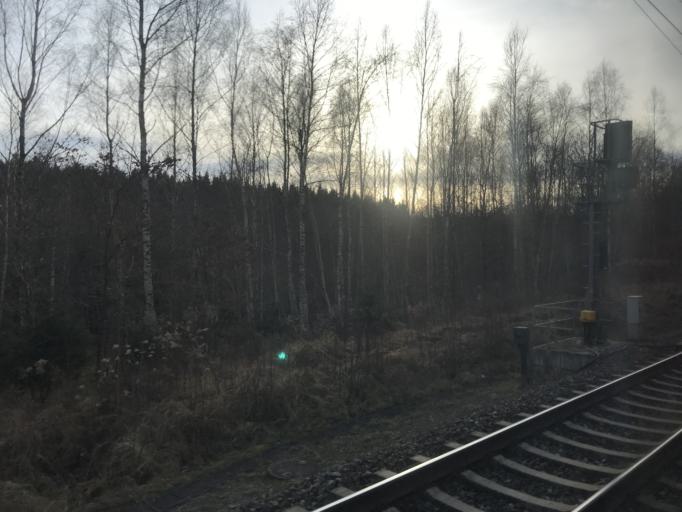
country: DE
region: Bavaria
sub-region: Swabia
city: Rosshaupten
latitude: 48.3948
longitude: 10.4799
